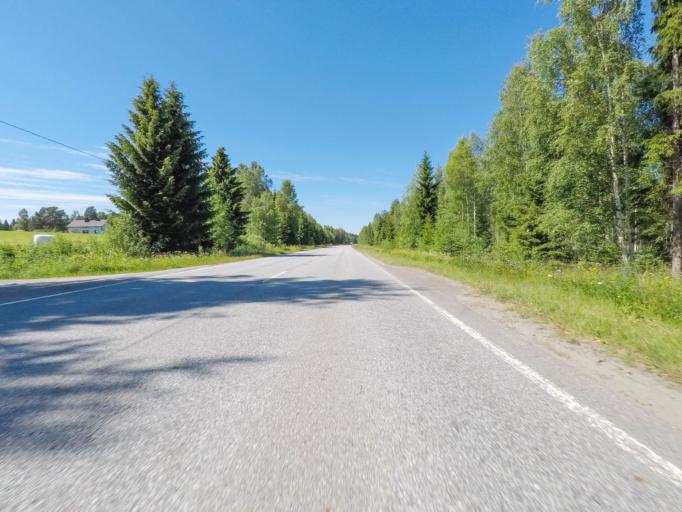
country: FI
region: Southern Savonia
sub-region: Savonlinna
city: Rantasalmi
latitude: 62.0305
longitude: 28.3417
